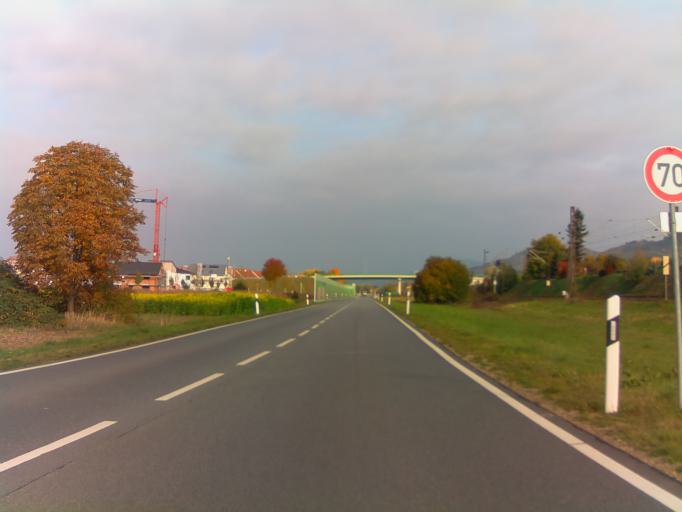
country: DE
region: Baden-Wuerttemberg
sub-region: Karlsruhe Region
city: Laudenbach
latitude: 49.6050
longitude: 8.6456
